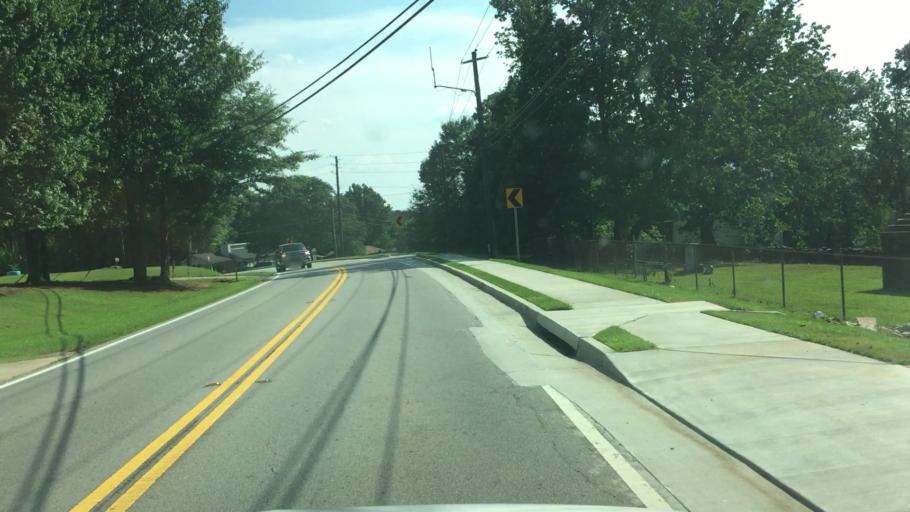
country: US
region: Georgia
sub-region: Gwinnett County
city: Dacula
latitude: 33.9823
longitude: -83.8934
